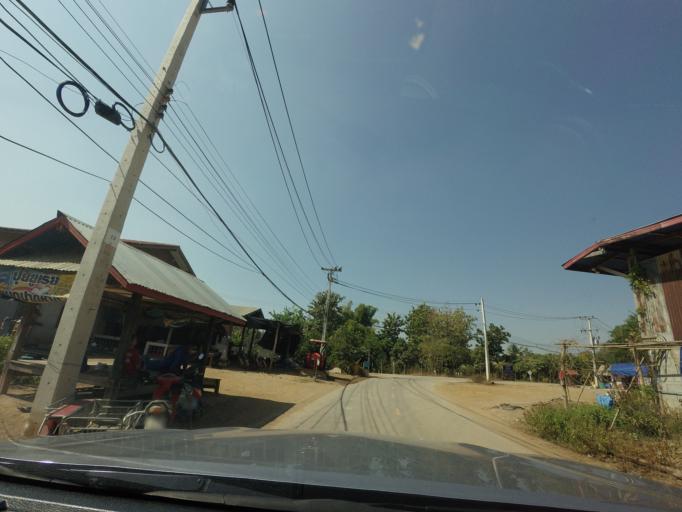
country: TH
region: Sukhothai
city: Si Samrong
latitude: 17.2182
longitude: 99.7766
